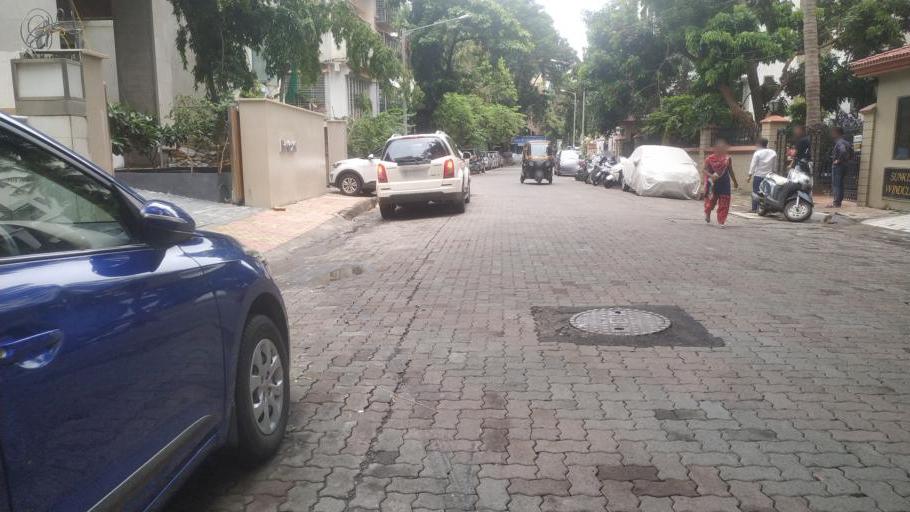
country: IN
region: Maharashtra
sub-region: Mumbai Suburban
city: Mumbai
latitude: 19.0588
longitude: 72.8329
